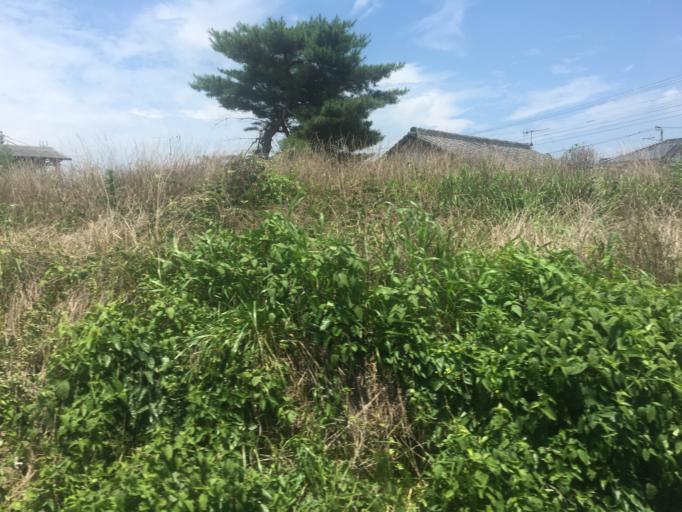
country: JP
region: Saitama
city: Kodamacho-kodamaminami
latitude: 36.1891
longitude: 139.1395
